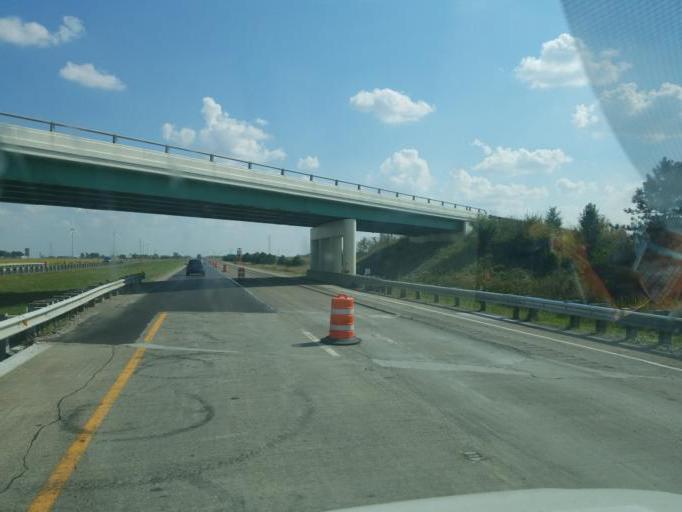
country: US
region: Ohio
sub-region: Van Wert County
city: Convoy
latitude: 40.9348
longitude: -84.6993
